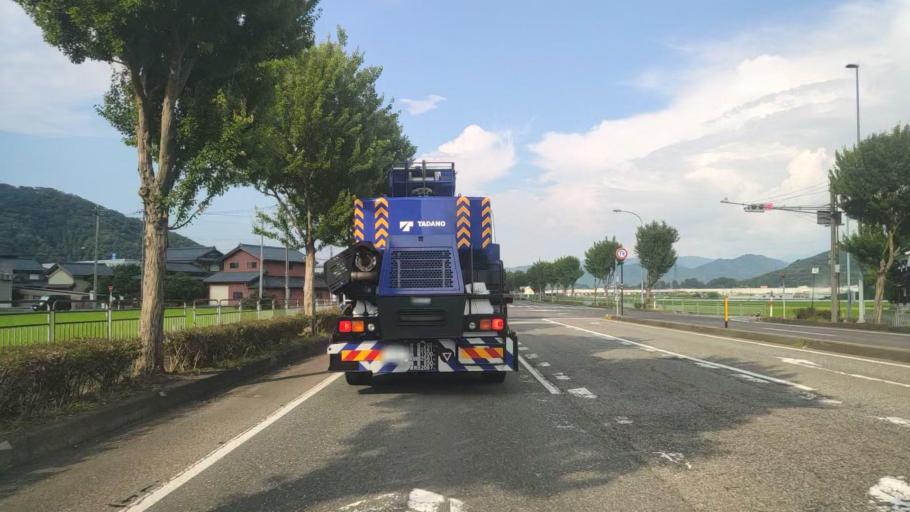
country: JP
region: Fukui
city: Takefu
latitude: 35.8847
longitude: 136.1835
